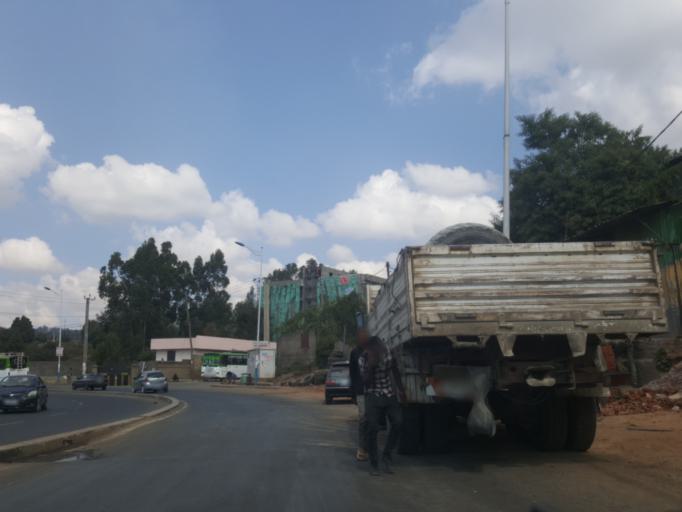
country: ET
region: Adis Abeba
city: Addis Ababa
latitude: 9.0554
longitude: 38.7176
